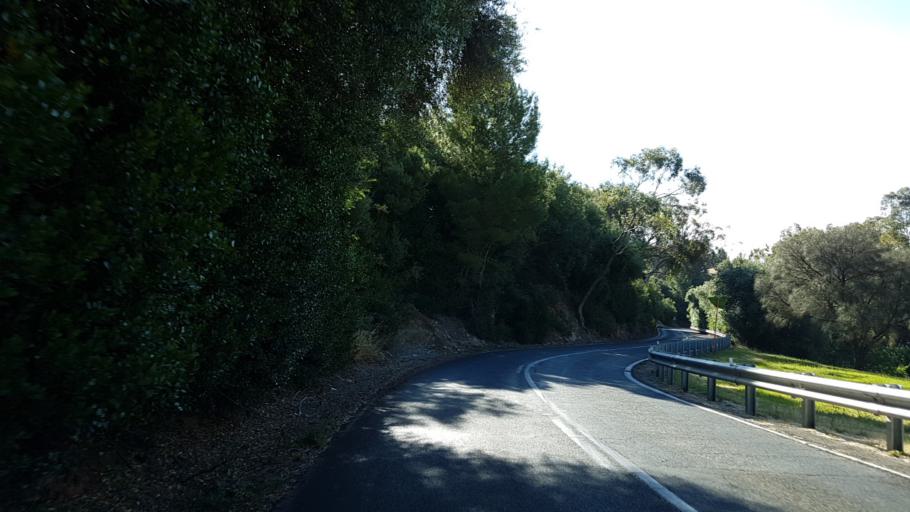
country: AU
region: South Australia
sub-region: Adelaide Hills
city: Adelaide Hills
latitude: -34.9126
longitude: 138.6967
